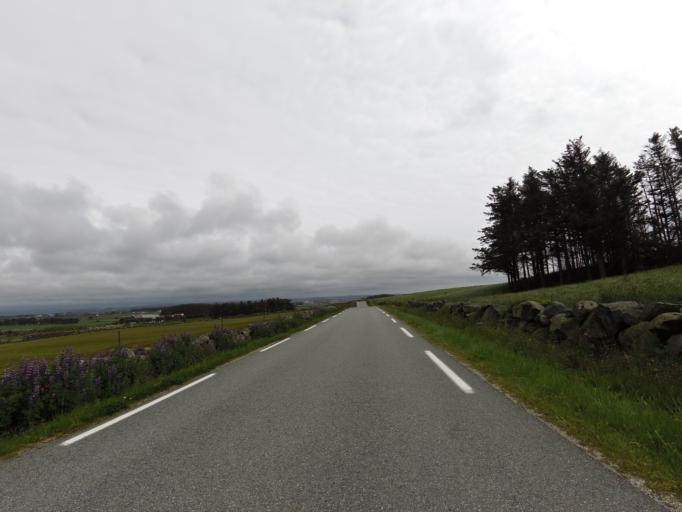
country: NO
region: Rogaland
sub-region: Ha
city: Naerbo
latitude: 58.6587
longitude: 5.5634
